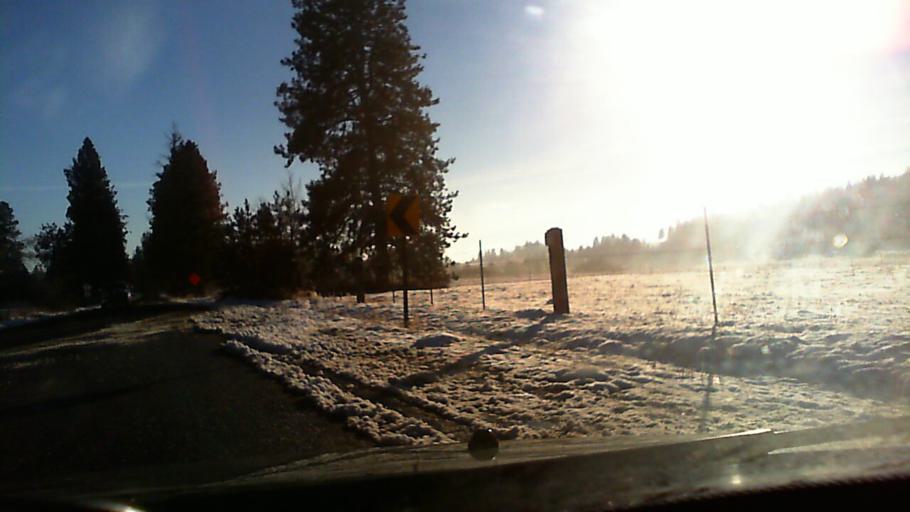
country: US
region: Washington
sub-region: Spokane County
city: Trentwood
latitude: 47.7290
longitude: -117.2131
